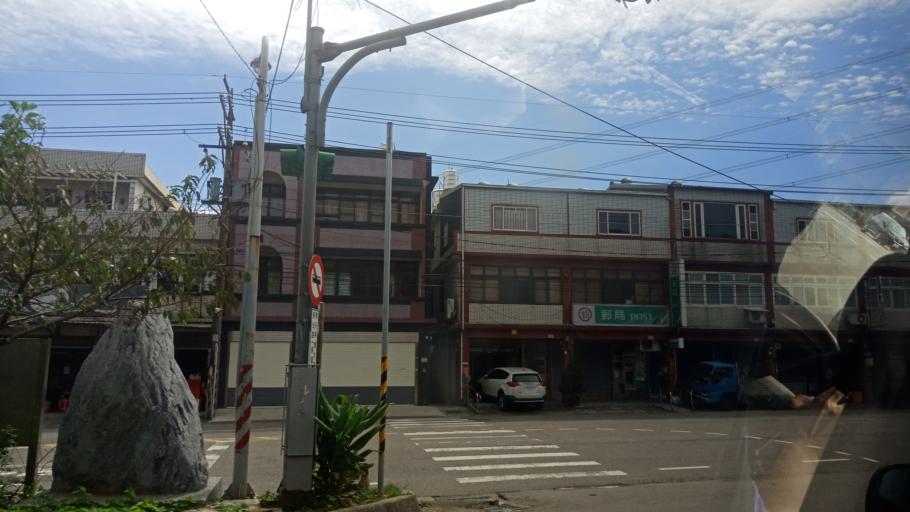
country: TW
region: Taiwan
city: Daxi
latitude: 24.8319
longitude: 121.2439
